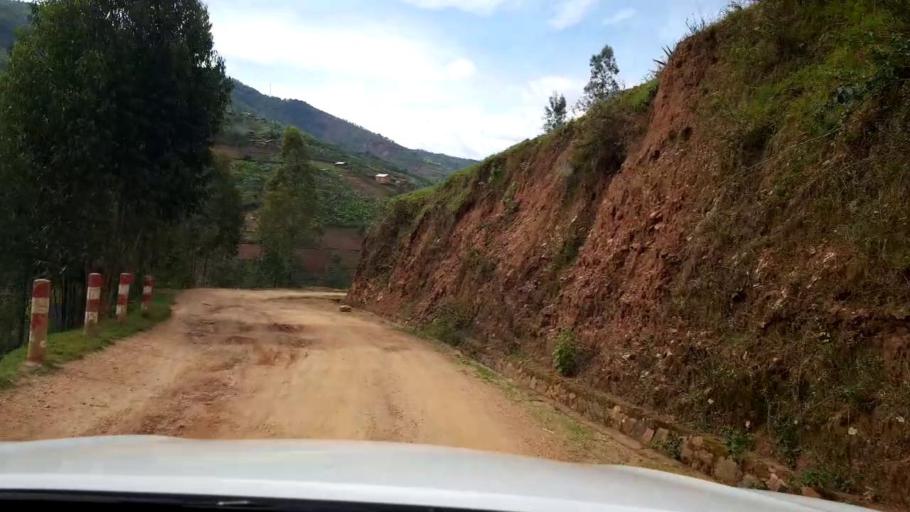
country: RW
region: Southern Province
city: Gitarama
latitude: -1.9787
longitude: 29.7088
